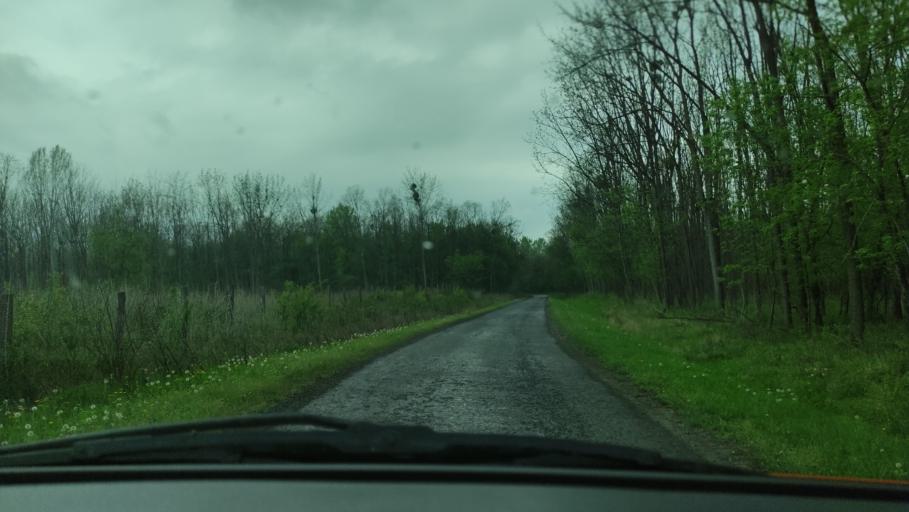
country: HU
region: Baranya
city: Mohacs
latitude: 45.9099
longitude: 18.7536
